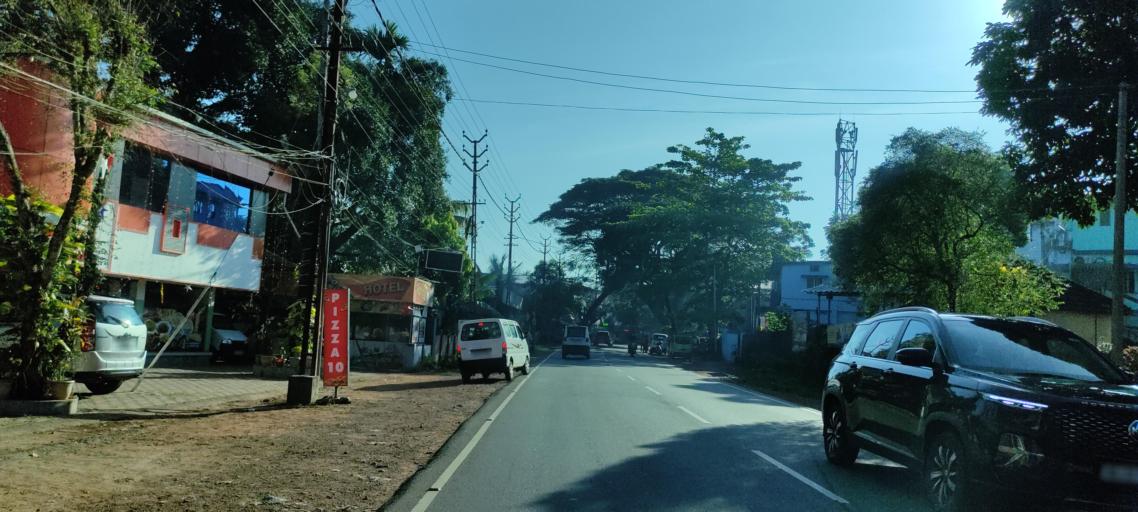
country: IN
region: Kerala
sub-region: Alappuzha
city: Kattanam
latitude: 9.1767
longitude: 76.5684
